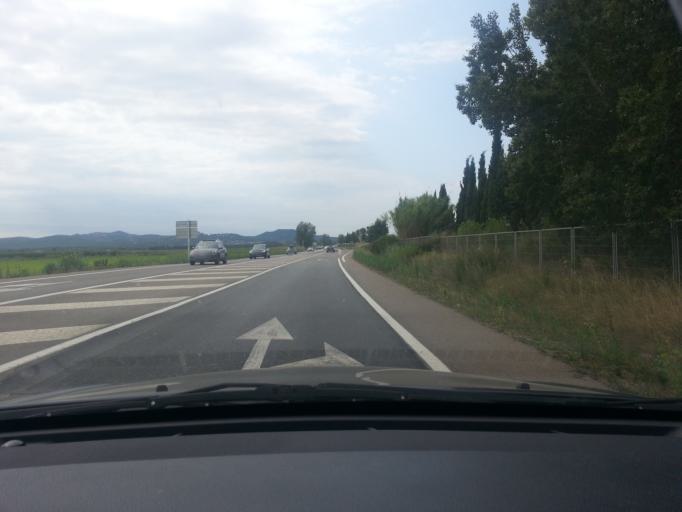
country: ES
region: Catalonia
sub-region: Provincia de Girona
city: Torroella de Montgri
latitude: 42.0184
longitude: 3.1416
